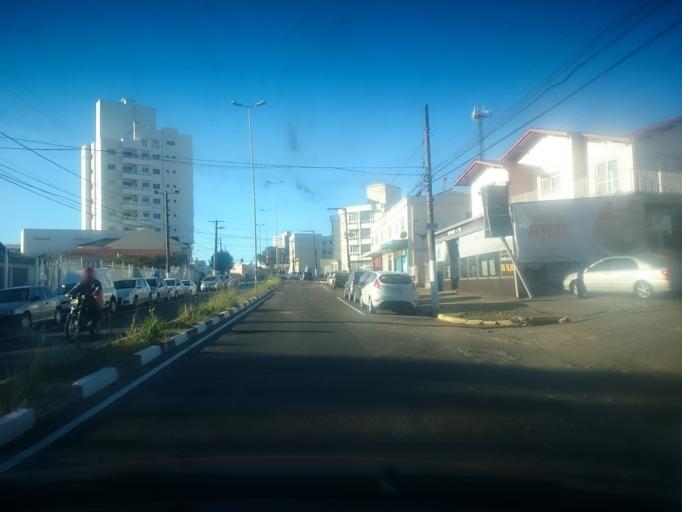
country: BR
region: Santa Catarina
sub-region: Lages
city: Lages
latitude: -27.8084
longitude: -50.3083
